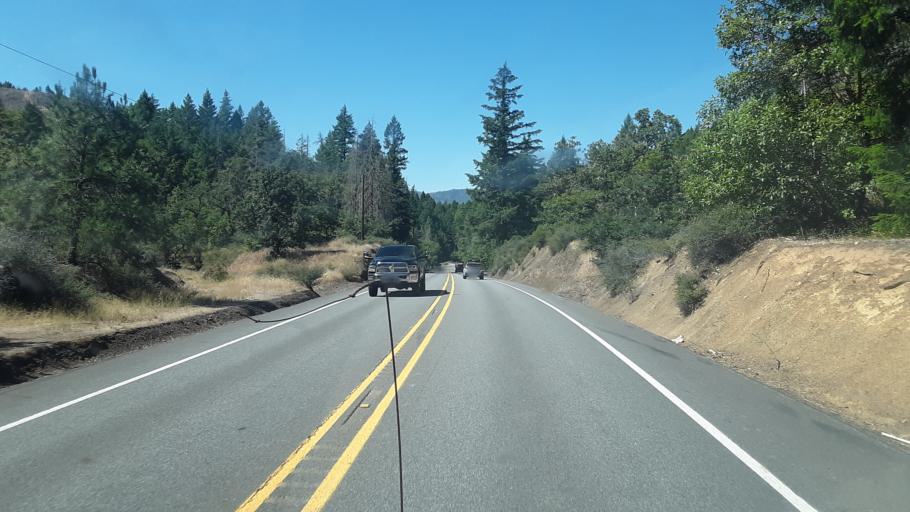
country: US
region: Oregon
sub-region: Josephine County
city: Cave Junction
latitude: 42.2523
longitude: -123.6259
